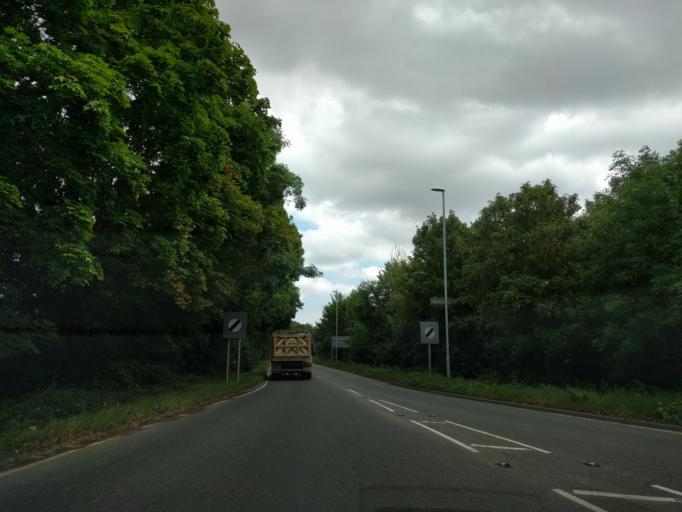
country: GB
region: England
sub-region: Cambridgeshire
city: Hemingford Grey
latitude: 52.3241
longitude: -0.0685
